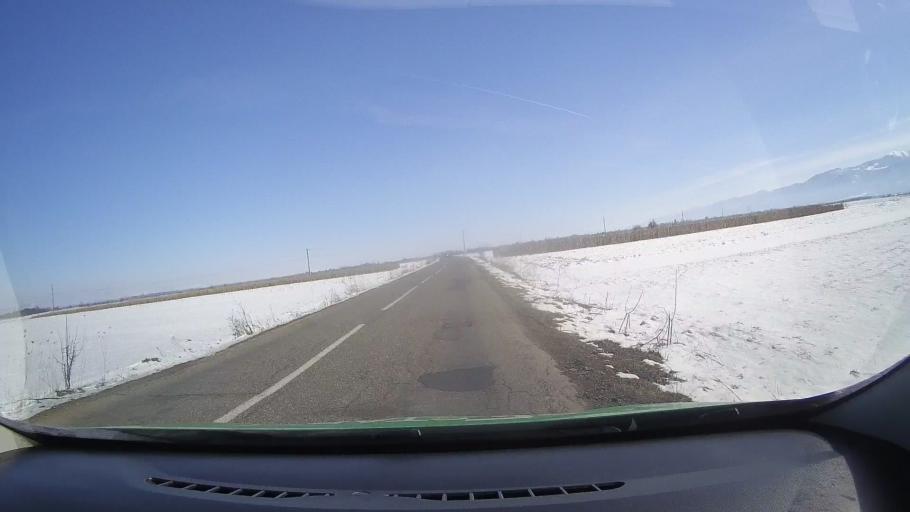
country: RO
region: Brasov
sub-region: Comuna Lisa
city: Lisa
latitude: 45.7269
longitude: 24.8794
